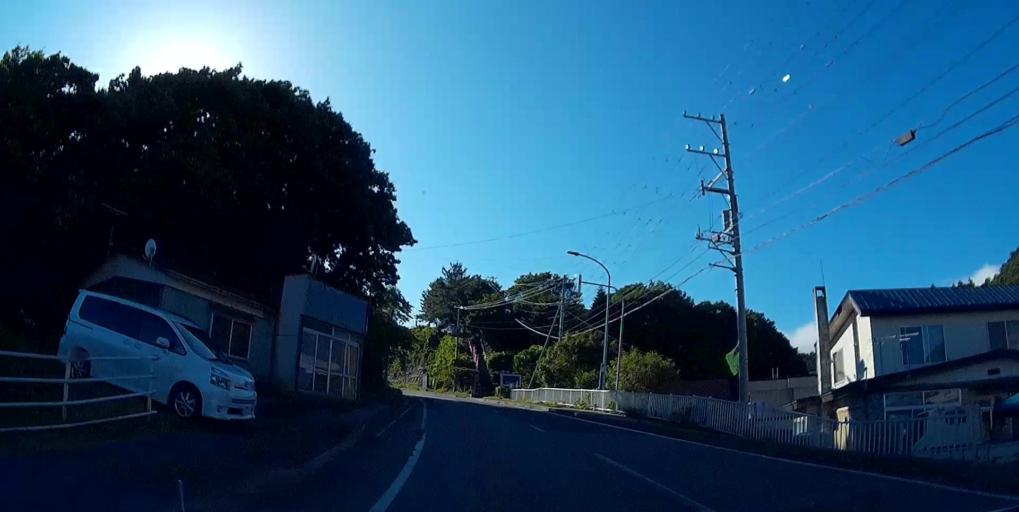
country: JP
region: Hokkaido
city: Kamiiso
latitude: 42.2247
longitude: 139.8257
